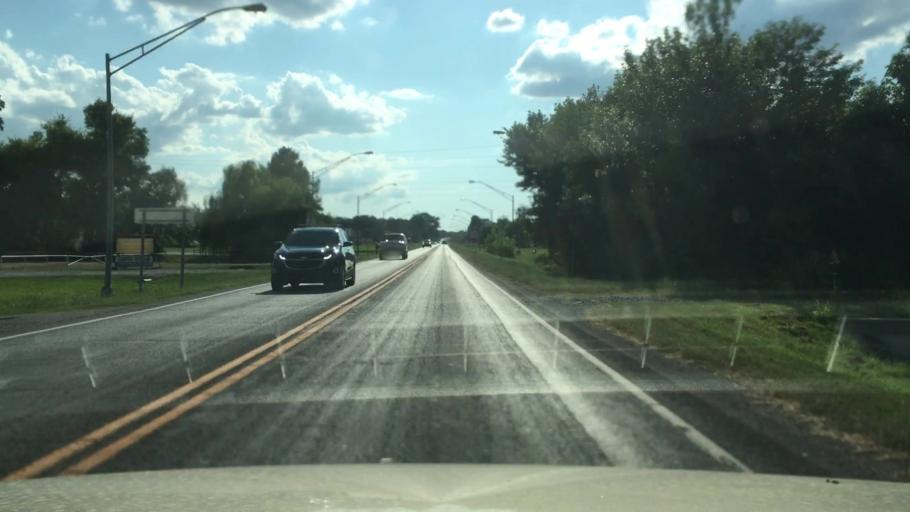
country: US
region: Oklahoma
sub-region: Cherokee County
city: Tahlequah
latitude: 35.9203
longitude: -95.0060
